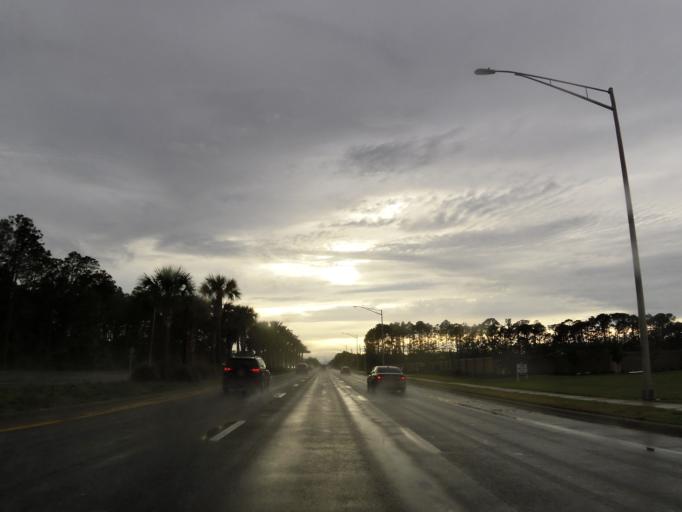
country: US
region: Florida
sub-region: Duval County
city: Jacksonville Beach
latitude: 30.2877
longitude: -81.4693
